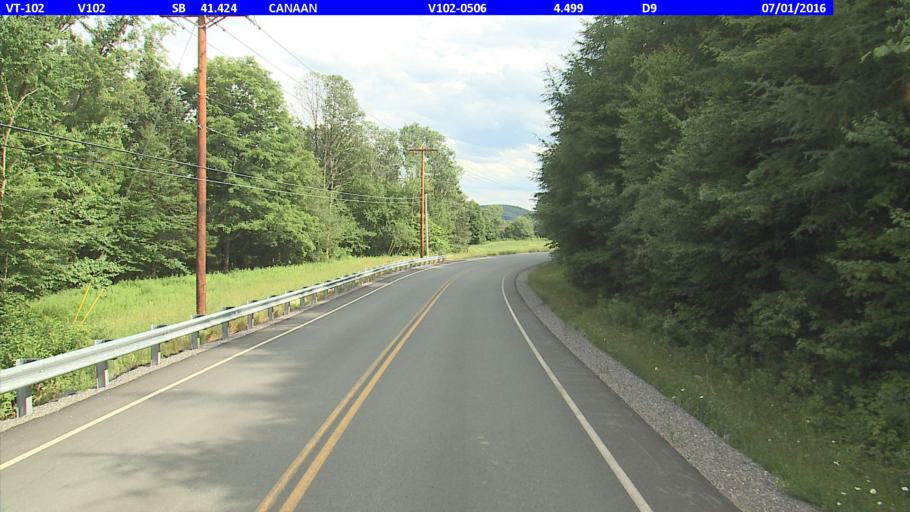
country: US
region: New Hampshire
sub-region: Coos County
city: Colebrook
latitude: 44.9694
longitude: -71.5260
